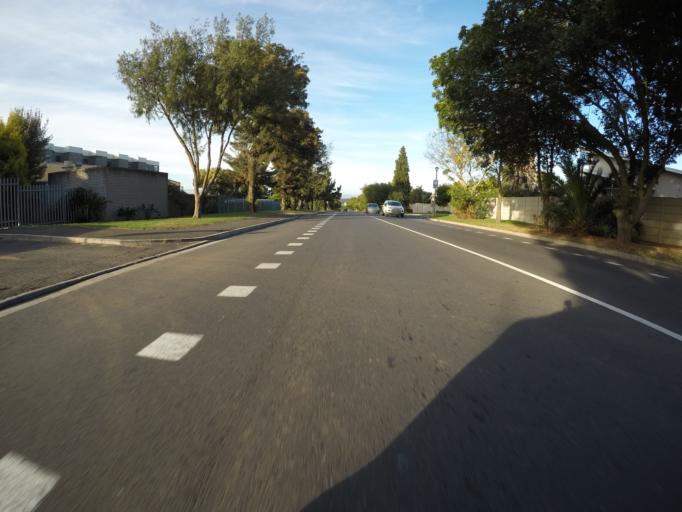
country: ZA
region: Western Cape
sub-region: City of Cape Town
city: Kraaifontein
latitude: -33.8670
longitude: 18.6528
